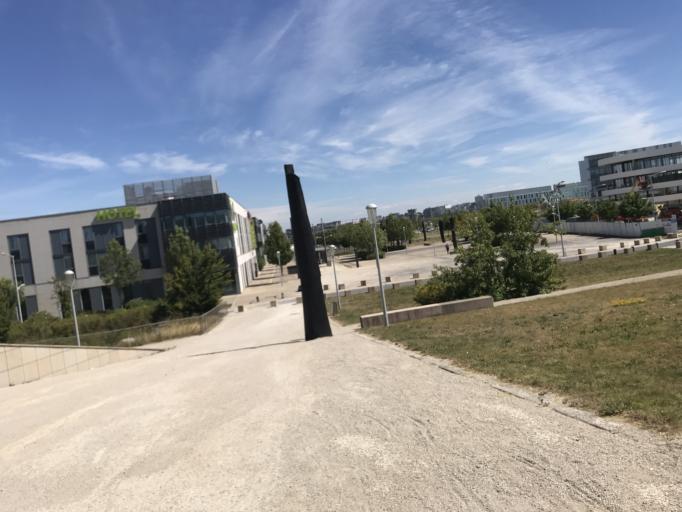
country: FR
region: Champagne-Ardenne
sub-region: Departement de la Marne
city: Bezannes
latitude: 49.2154
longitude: 3.9955
